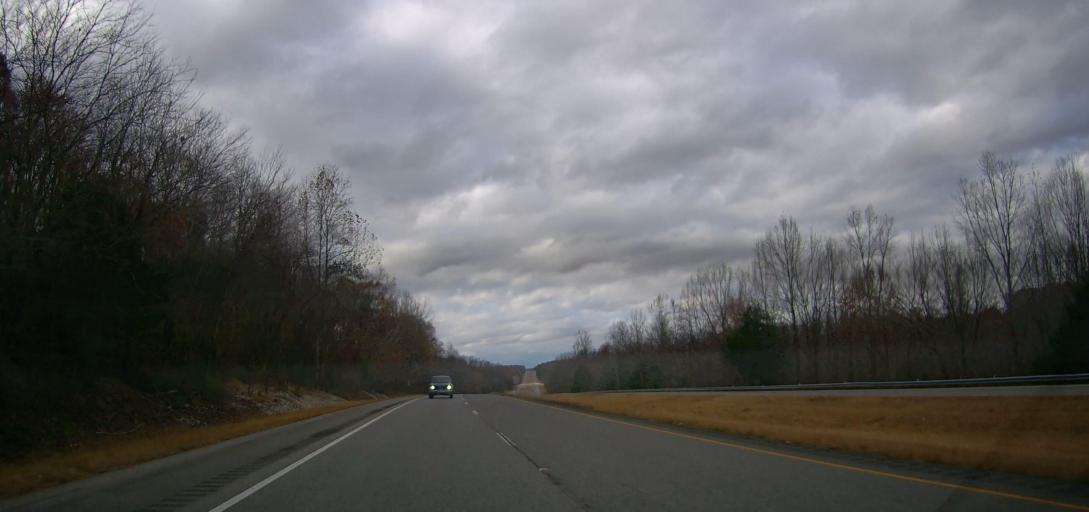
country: US
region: Alabama
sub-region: Lawrence County
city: Town Creek
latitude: 34.6027
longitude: -87.4468
